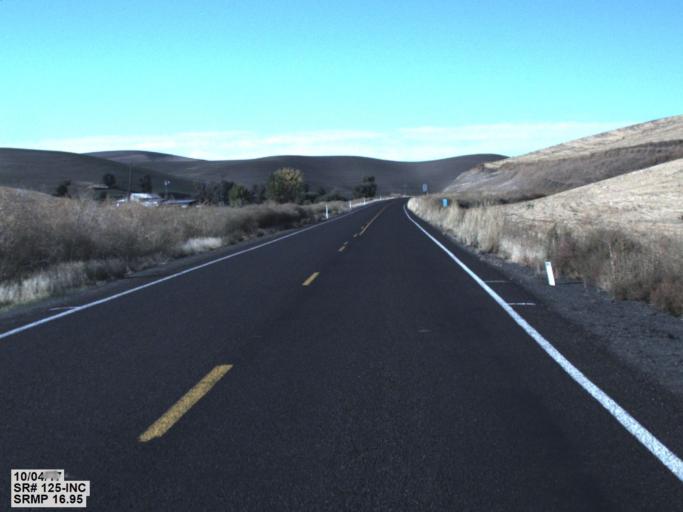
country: US
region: Washington
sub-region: Walla Walla County
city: Walla Walla
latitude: 46.2124
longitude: -118.3913
